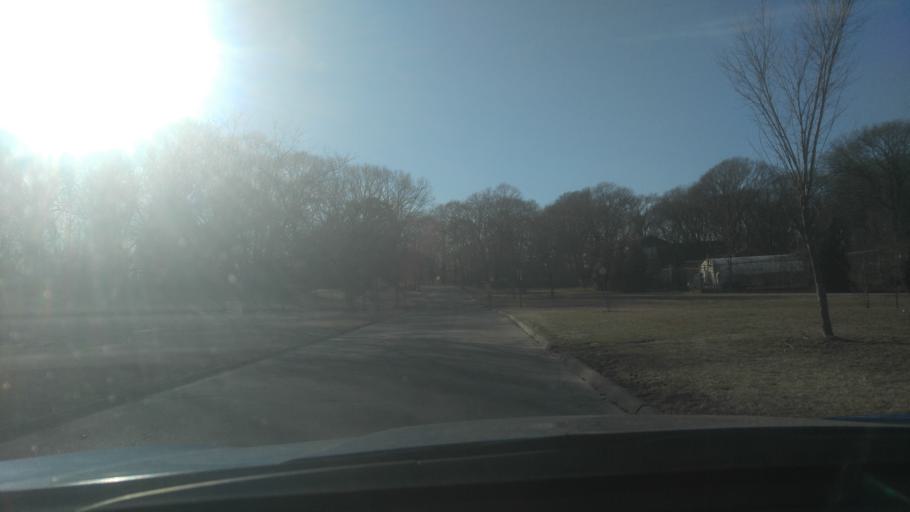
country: US
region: Rhode Island
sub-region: Kent County
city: Warwick
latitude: 41.6966
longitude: -71.4186
